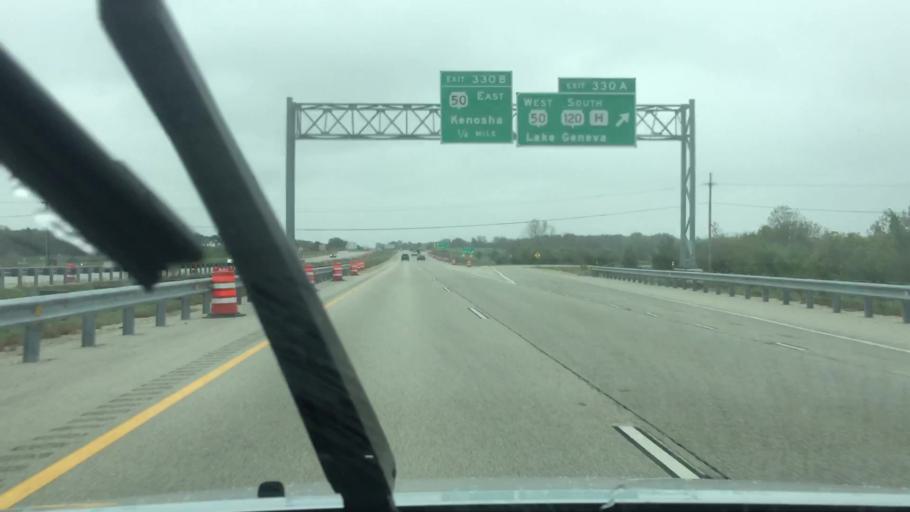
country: US
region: Wisconsin
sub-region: Walworth County
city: Lake Geneva
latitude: 42.5979
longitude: -88.4121
